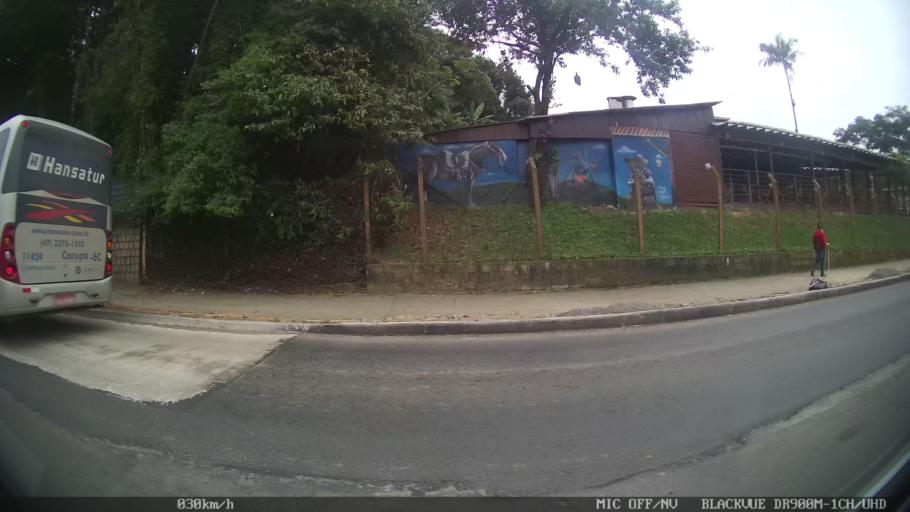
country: BR
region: Santa Catarina
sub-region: Joinville
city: Joinville
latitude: -26.3010
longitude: -48.8242
